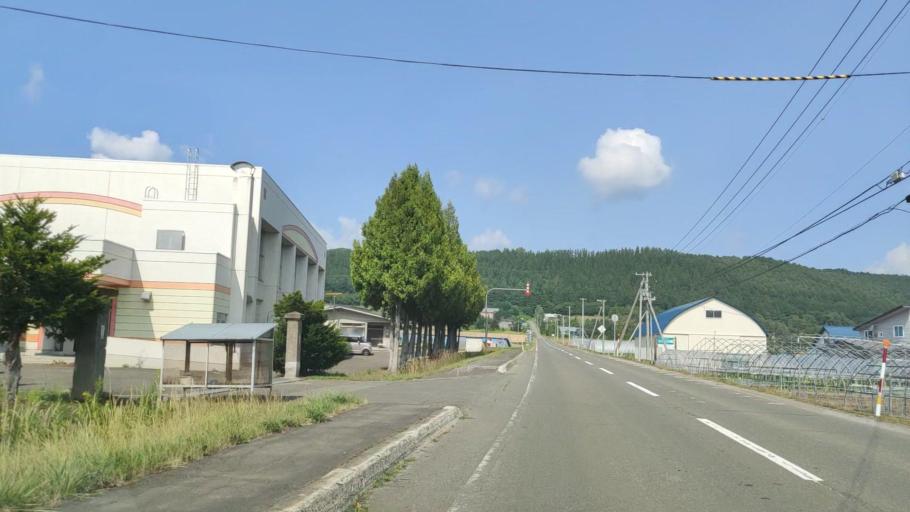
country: JP
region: Hokkaido
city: Shimo-furano
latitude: 43.3930
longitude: 142.3949
